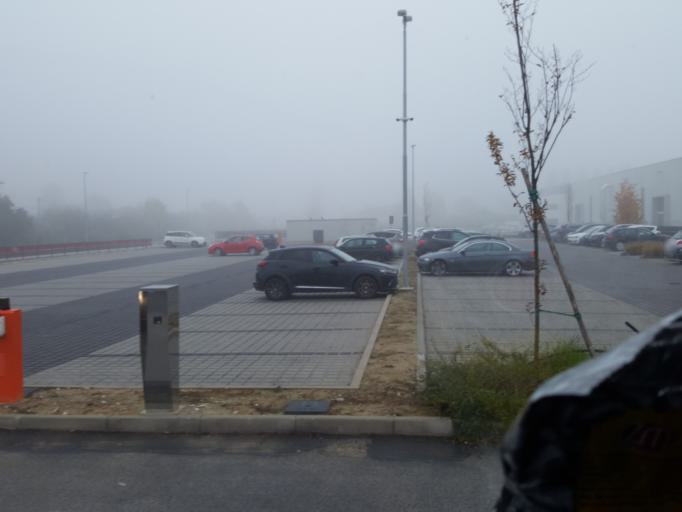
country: IT
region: Veneto
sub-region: Provincia di Padova
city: Borgoricco-San Michele delle Badesse-Sant'Eufemia
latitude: 45.5398
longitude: 11.9507
